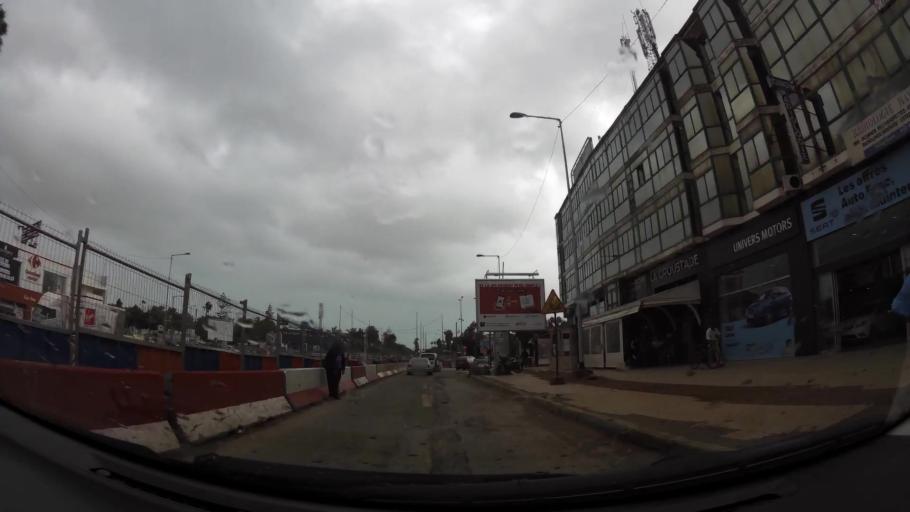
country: MA
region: Grand Casablanca
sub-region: Casablanca
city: Casablanca
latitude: 33.5768
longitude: -7.6742
